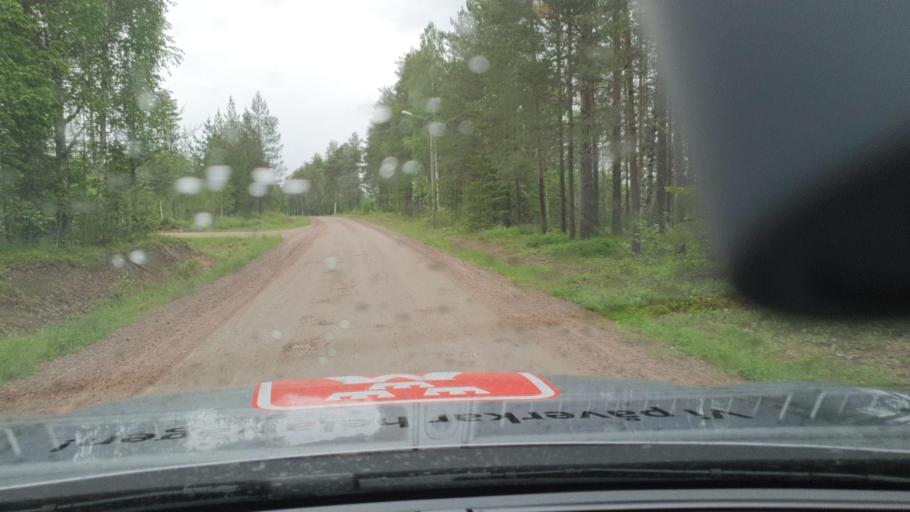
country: SE
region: Norrbotten
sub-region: Overkalix Kommun
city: OEverkalix
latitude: 66.4976
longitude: 22.7618
